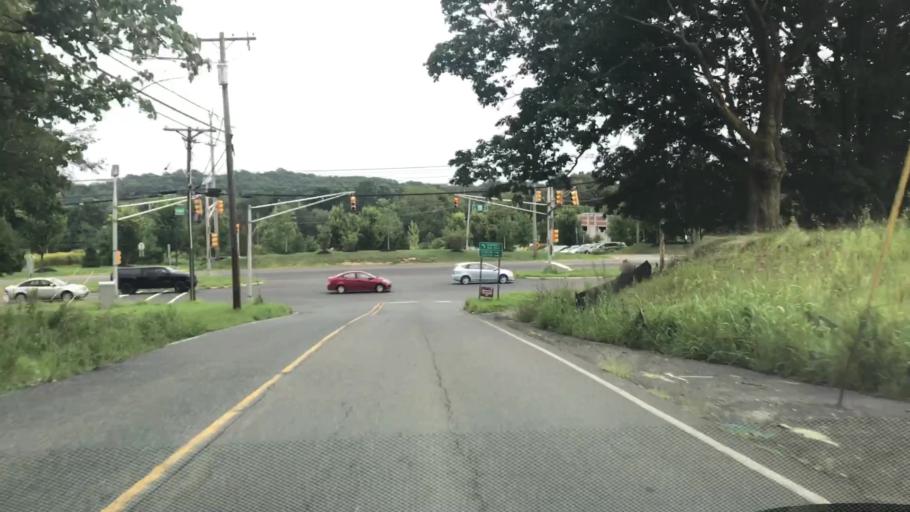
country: US
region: New Jersey
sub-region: Hunterdon County
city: Annandale
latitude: 40.6434
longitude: -74.8605
